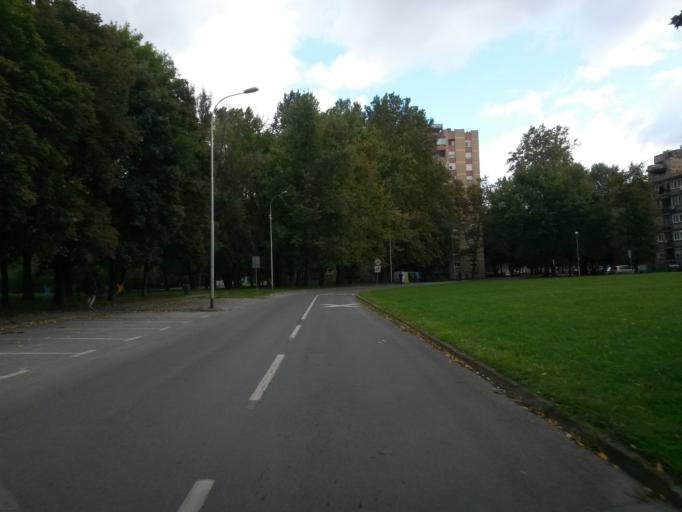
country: HR
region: Osjecko-Baranjska
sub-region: Grad Osijek
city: Osijek
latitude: 45.5533
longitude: 18.6985
